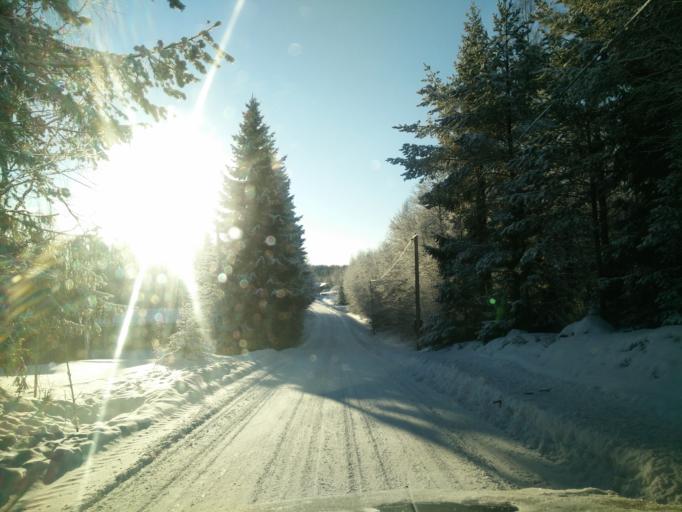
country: SE
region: Vaesternorrland
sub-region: Sundsvalls Kommun
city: Njurundabommen
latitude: 62.2276
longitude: 17.4980
